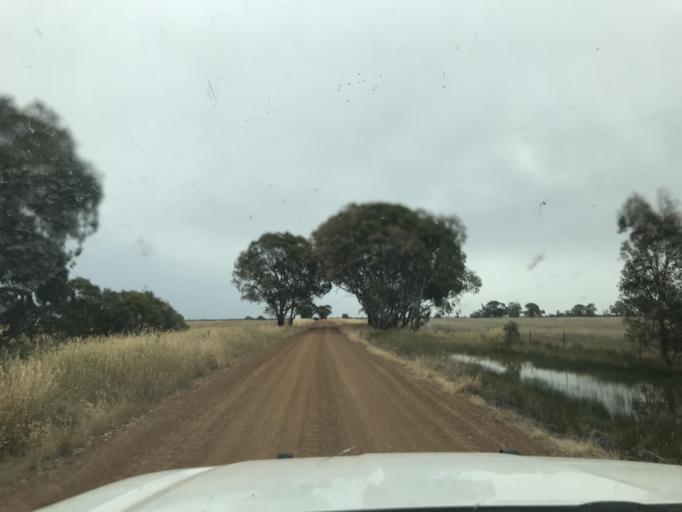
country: AU
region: Victoria
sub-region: Horsham
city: Horsham
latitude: -37.0617
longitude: 141.6223
